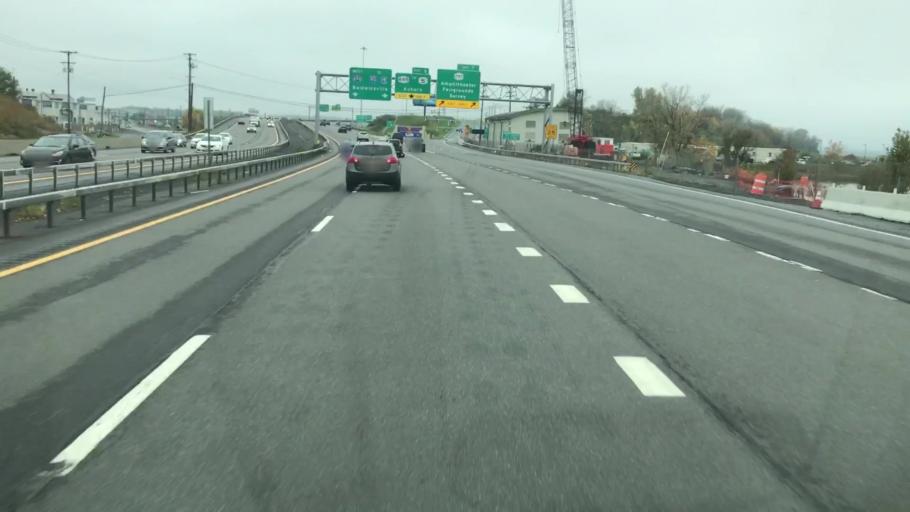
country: US
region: New York
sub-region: Onondaga County
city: Solvay
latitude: 43.0708
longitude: -76.2035
